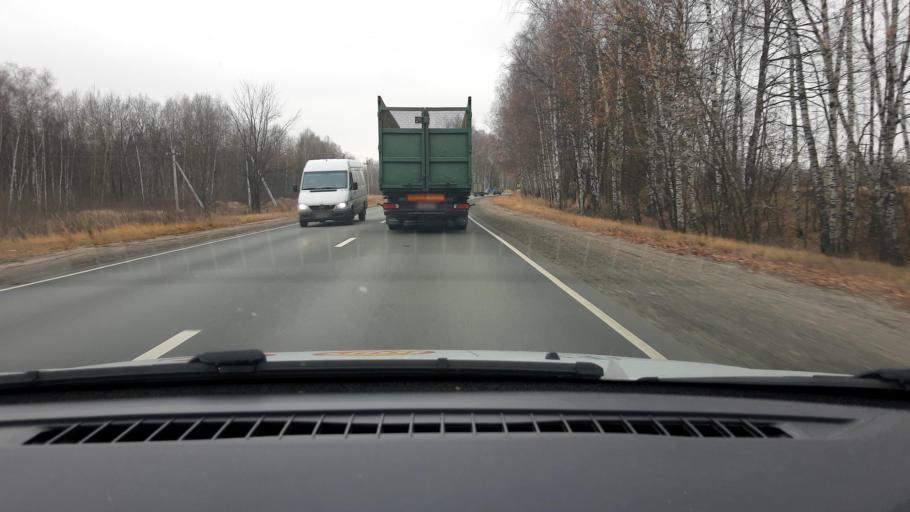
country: RU
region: Nizjnij Novgorod
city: Gorodets
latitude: 56.5765
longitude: 43.4748
